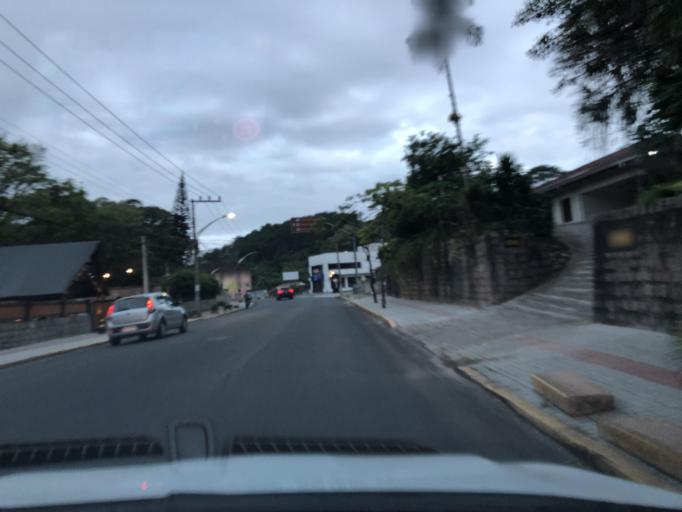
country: BR
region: Santa Catarina
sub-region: Joinville
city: Joinville
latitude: -26.2982
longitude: -48.8594
